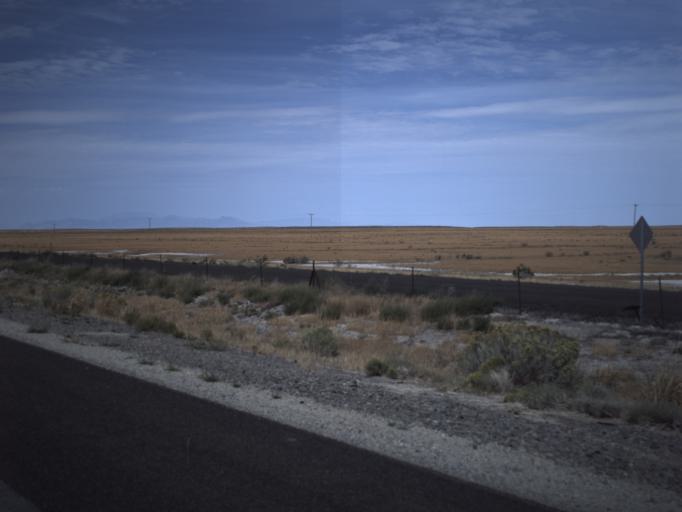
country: US
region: Utah
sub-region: Tooele County
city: Grantsville
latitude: 40.7267
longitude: -113.2032
